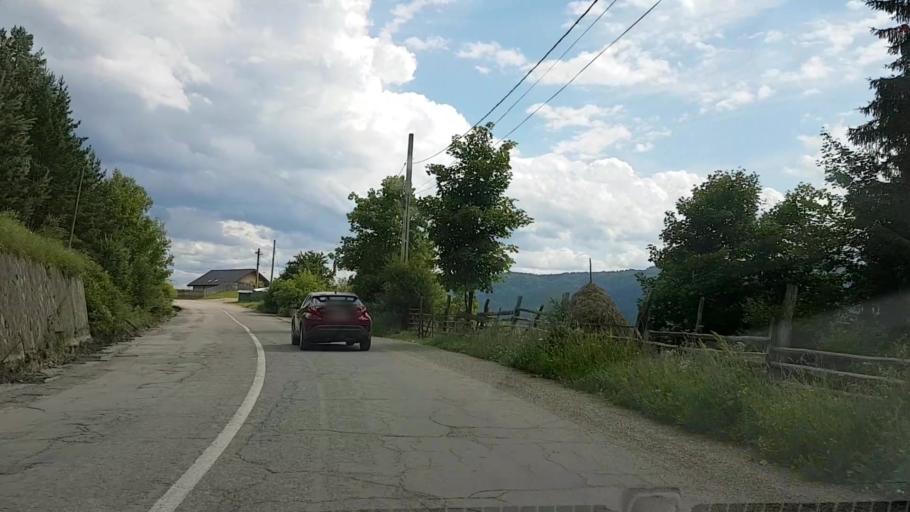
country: RO
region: Neamt
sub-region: Comuna Hangu
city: Hangu
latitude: 47.0486
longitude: 26.0395
